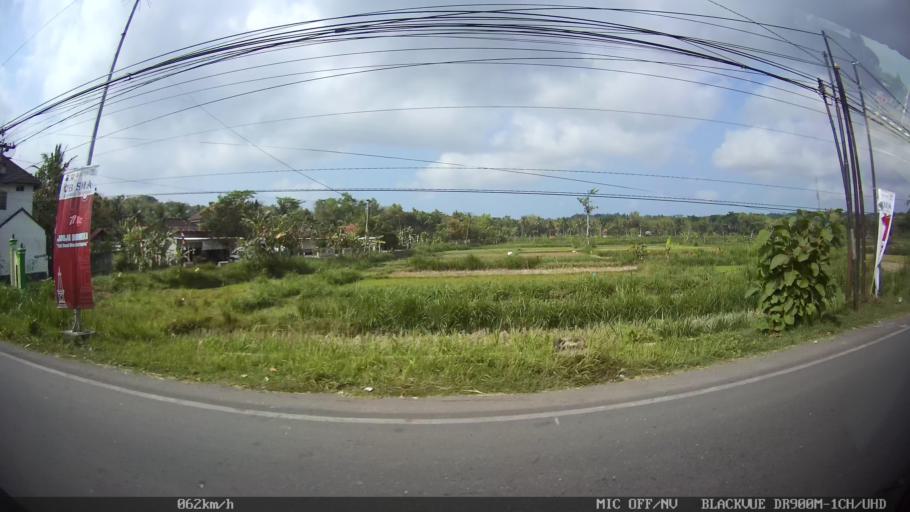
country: ID
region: Daerah Istimewa Yogyakarta
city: Srandakan
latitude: -7.8669
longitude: 110.1770
